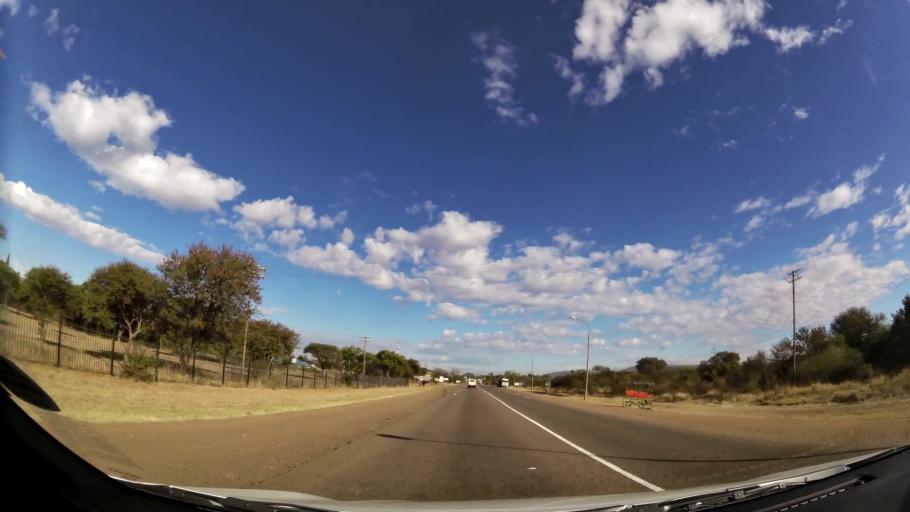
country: ZA
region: Limpopo
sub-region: Waterberg District Municipality
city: Bela-Bela
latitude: -24.8915
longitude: 28.3032
